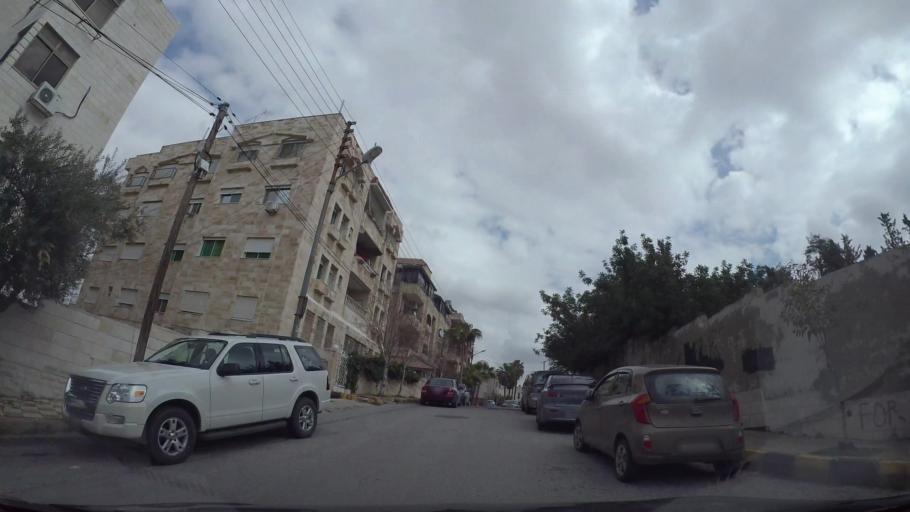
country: JO
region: Amman
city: Amman
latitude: 31.9763
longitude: 35.9002
